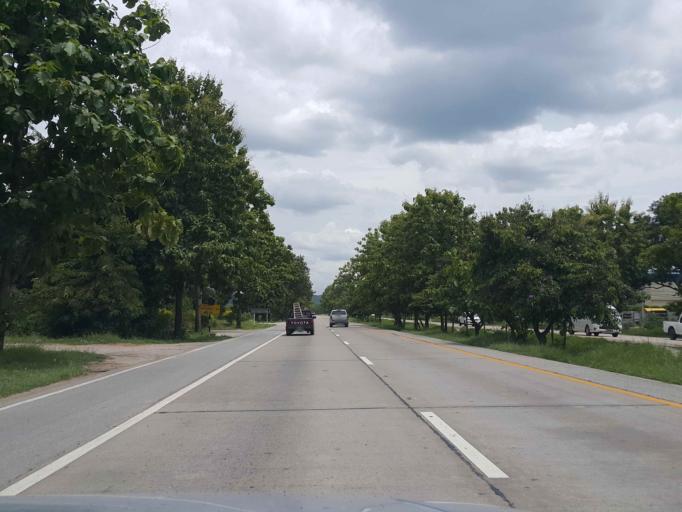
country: TH
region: Lamphun
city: Lamphun
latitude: 18.5339
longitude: 99.0763
